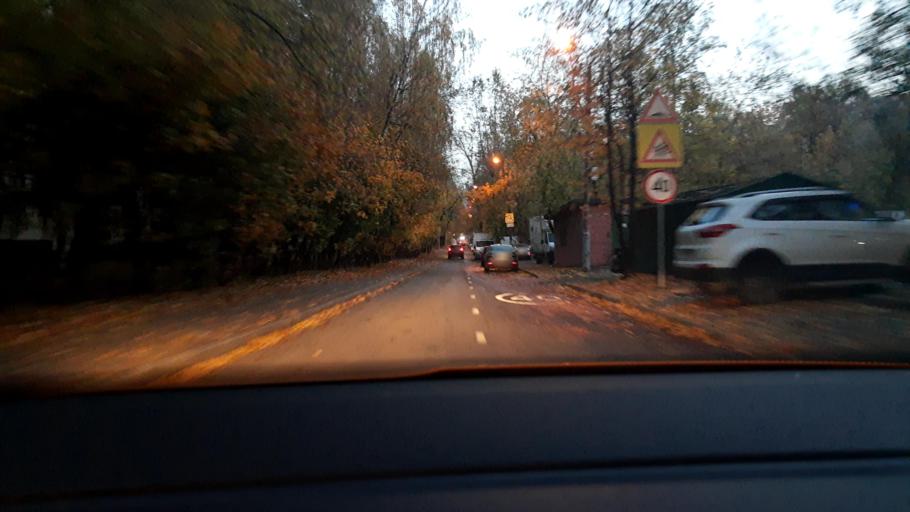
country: RU
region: Moscow
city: Gol'yanovo
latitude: 55.8117
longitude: 37.8265
